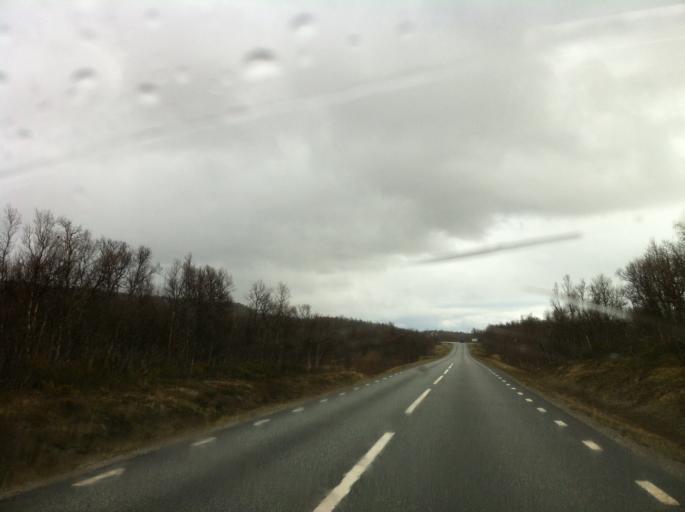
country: NO
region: Sor-Trondelag
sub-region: Tydal
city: Aas
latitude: 62.6268
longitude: 12.1285
